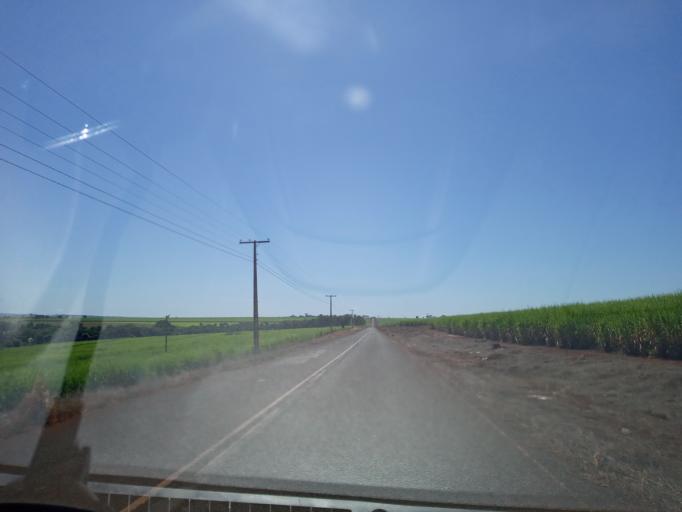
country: BR
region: Goias
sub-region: Itumbiara
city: Itumbiara
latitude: -18.4242
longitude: -49.1644
